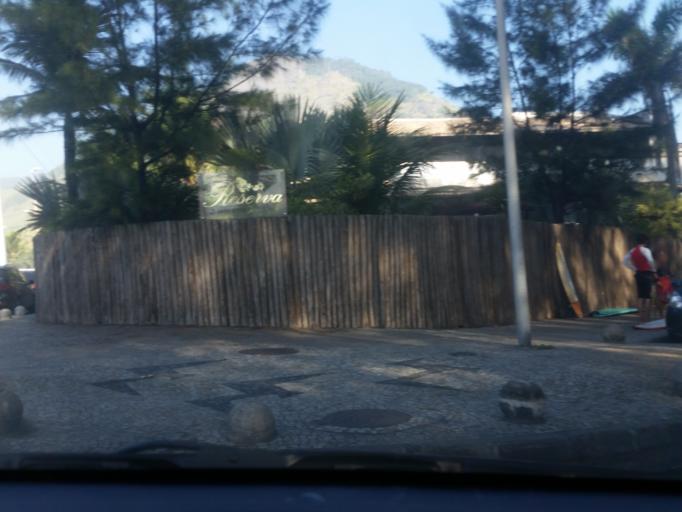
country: BR
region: Rio de Janeiro
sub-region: Nilopolis
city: Nilopolis
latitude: -23.0342
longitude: -43.4911
